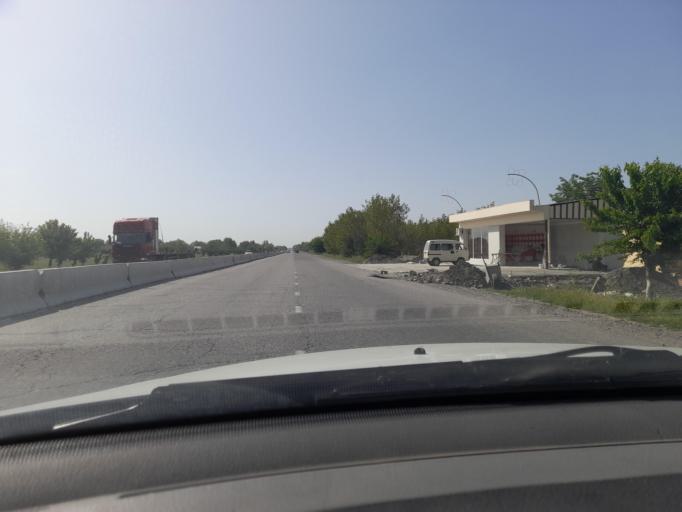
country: UZ
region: Samarqand
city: Chelak
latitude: 39.8465
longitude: 66.8088
